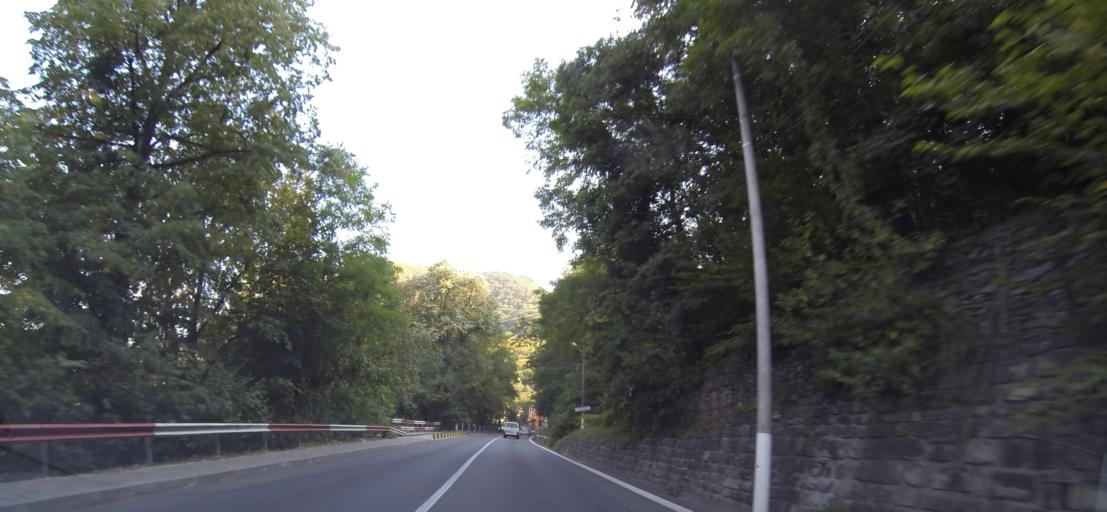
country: RO
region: Valcea
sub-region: Oras Calimanesti
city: Calimanesti
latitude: 45.2620
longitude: 24.3189
